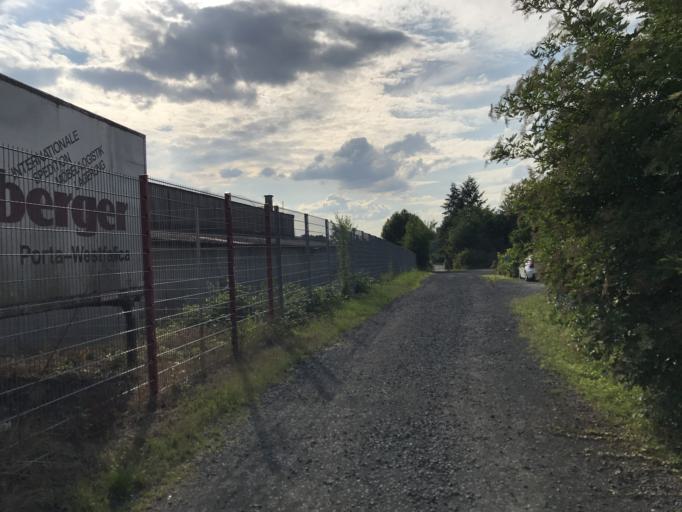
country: DE
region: Hesse
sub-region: Regierungsbezirk Giessen
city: Lich
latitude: 50.5139
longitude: 8.8308
